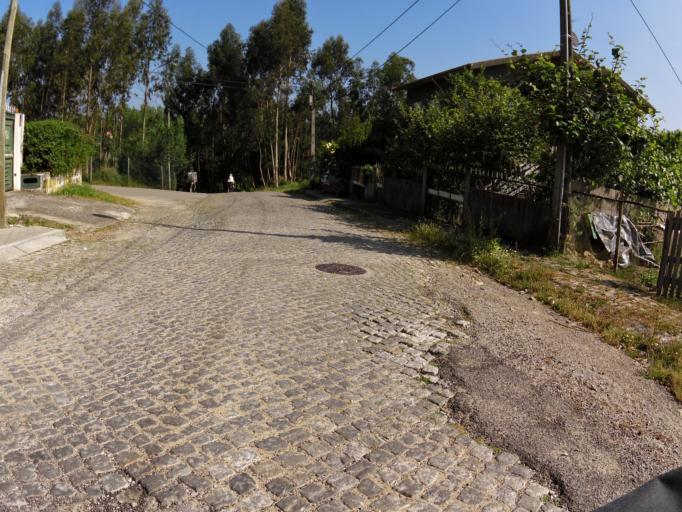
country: PT
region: Porto
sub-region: Vila Nova de Gaia
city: Olival
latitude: 41.0452
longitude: -8.5360
